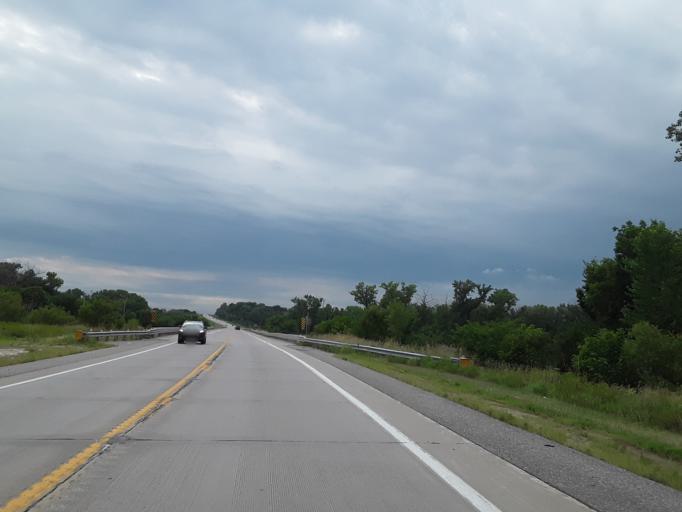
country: US
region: Nebraska
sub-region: Saunders County
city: Yutan
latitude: 41.2343
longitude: -96.3573
